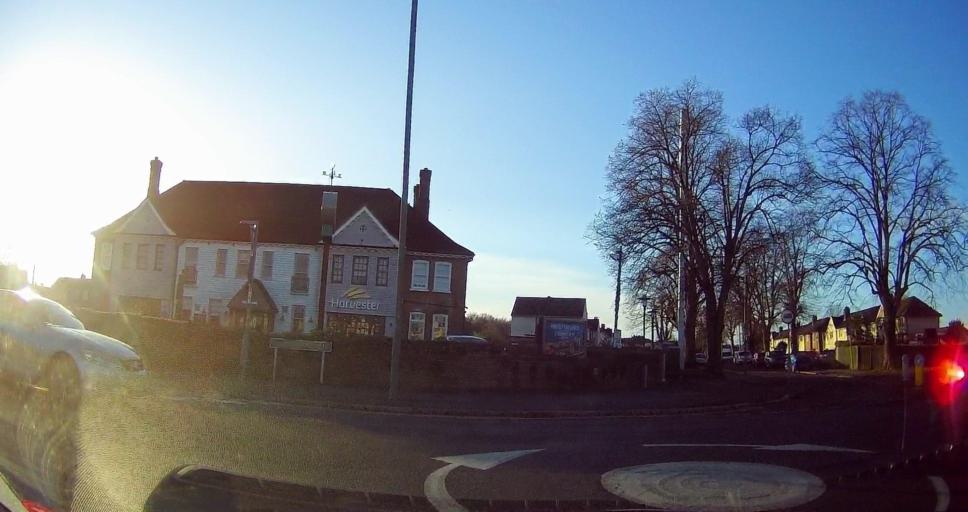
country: GB
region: England
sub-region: Greater London
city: Chislehurst
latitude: 51.3908
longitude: 0.0539
